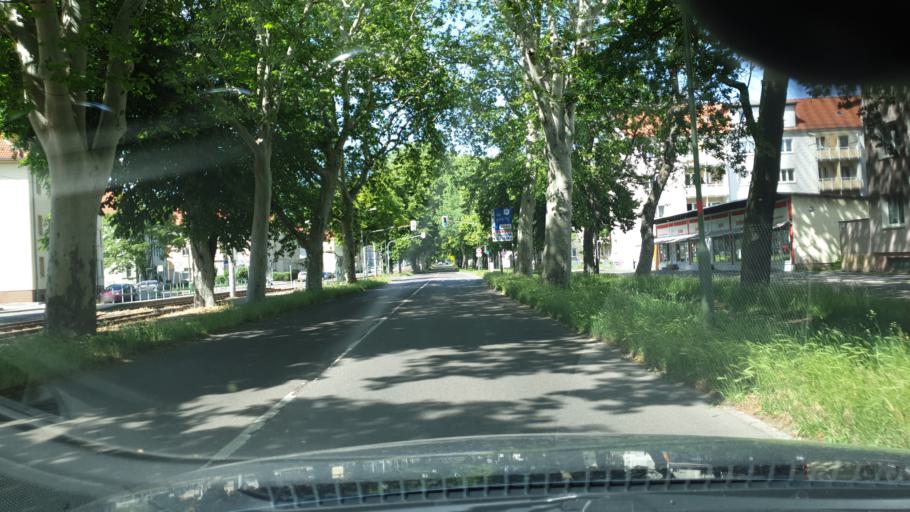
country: DE
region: Saxony-Anhalt
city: Dessau
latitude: 51.8021
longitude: 12.2409
